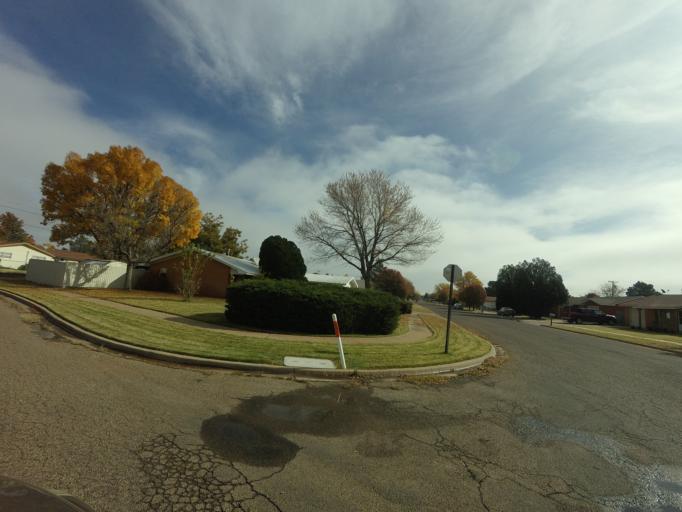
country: US
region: New Mexico
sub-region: Curry County
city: Clovis
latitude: 34.4239
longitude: -103.2172
